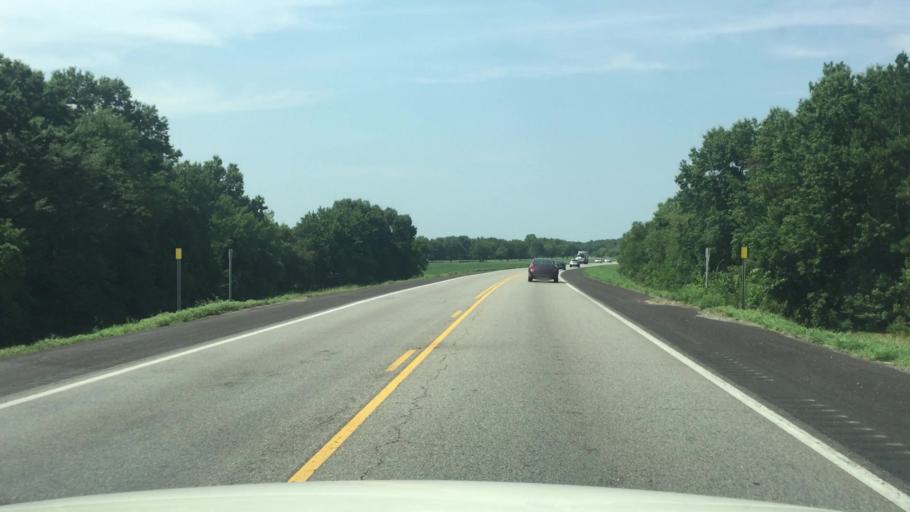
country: US
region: Kansas
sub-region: Crawford County
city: Pittsburg
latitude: 37.3903
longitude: -94.7147
